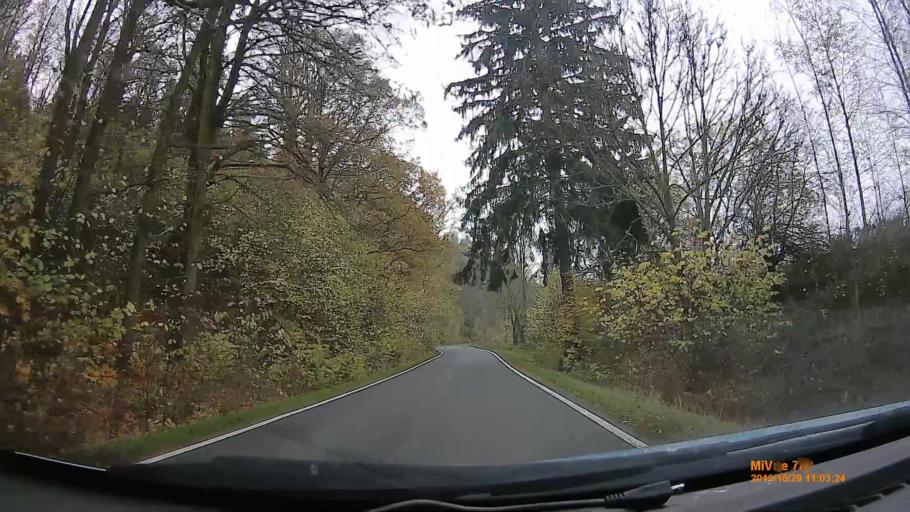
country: PL
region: Lower Silesian Voivodeship
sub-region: Powiat klodzki
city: Radkow
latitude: 50.4846
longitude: 16.4696
